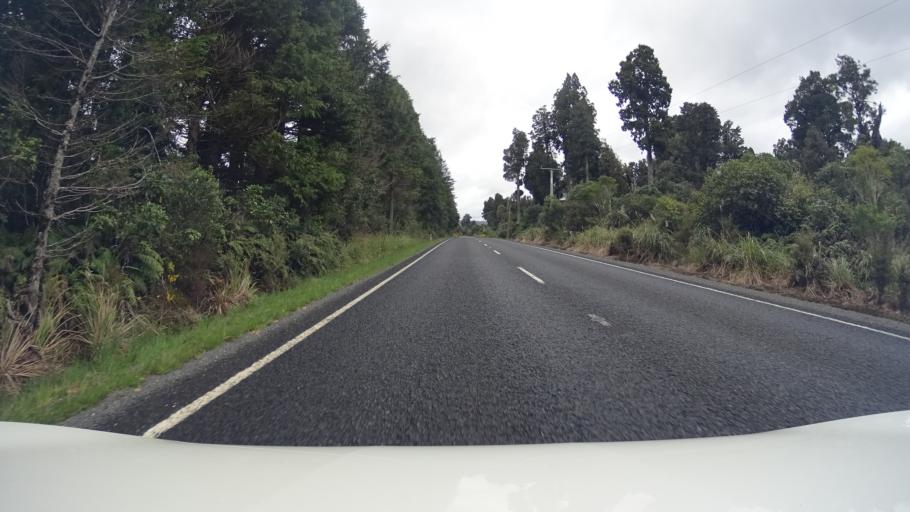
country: NZ
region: Manawatu-Wanganui
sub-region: Ruapehu District
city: Waiouru
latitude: -39.2401
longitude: 175.3917
